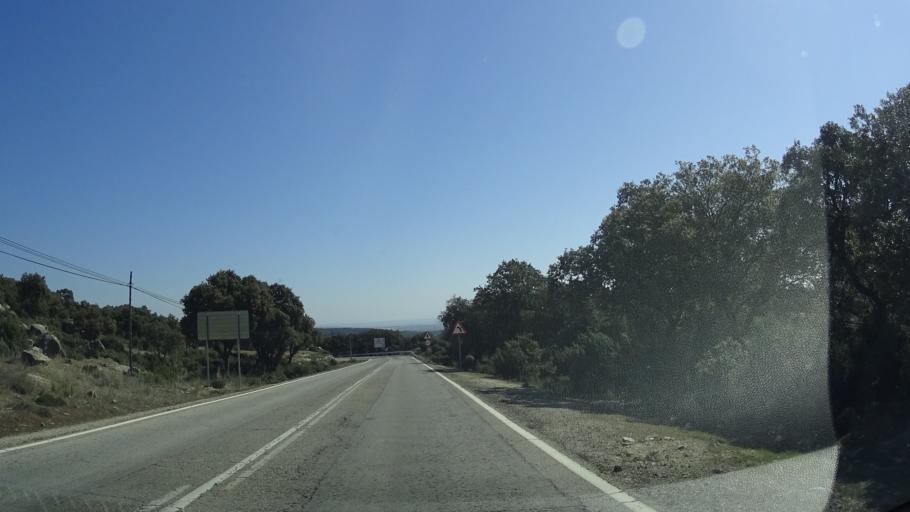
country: ES
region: Madrid
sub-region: Provincia de Madrid
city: Hoyo de Manzanares
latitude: 40.6214
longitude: -3.8899
